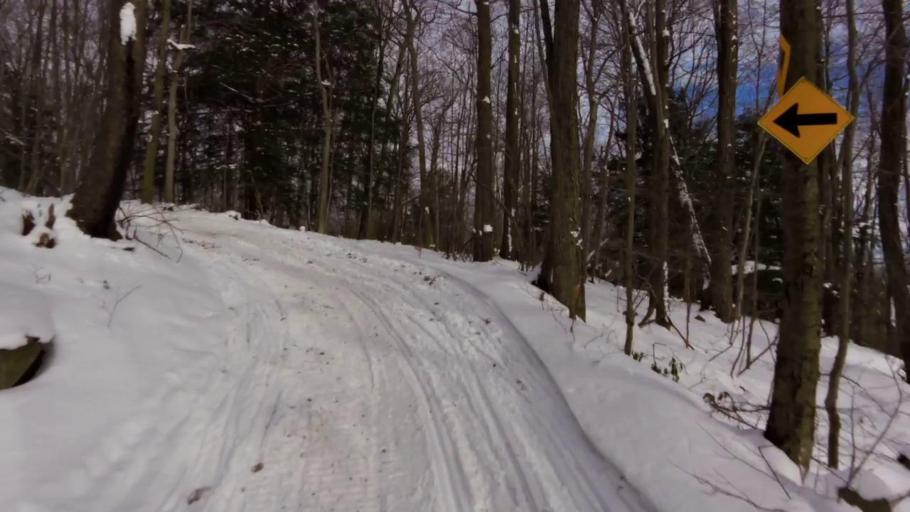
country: US
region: Pennsylvania
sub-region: McKean County
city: Foster Brook
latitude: 42.0153
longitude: -78.5521
